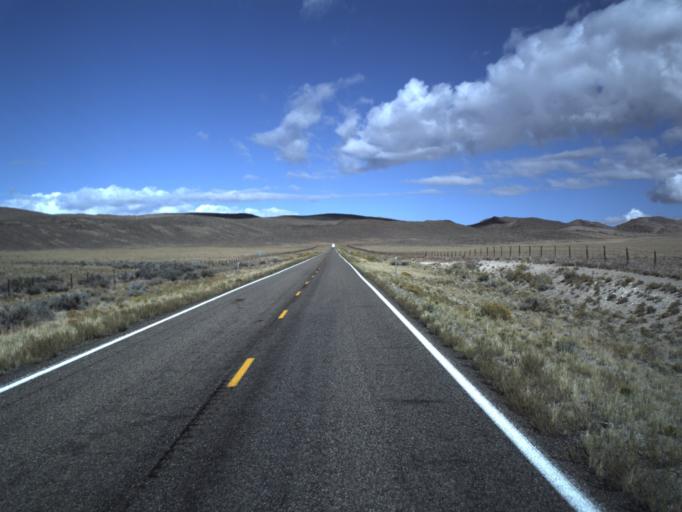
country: US
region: Utah
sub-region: Beaver County
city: Milford
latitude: 38.5933
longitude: -113.8227
